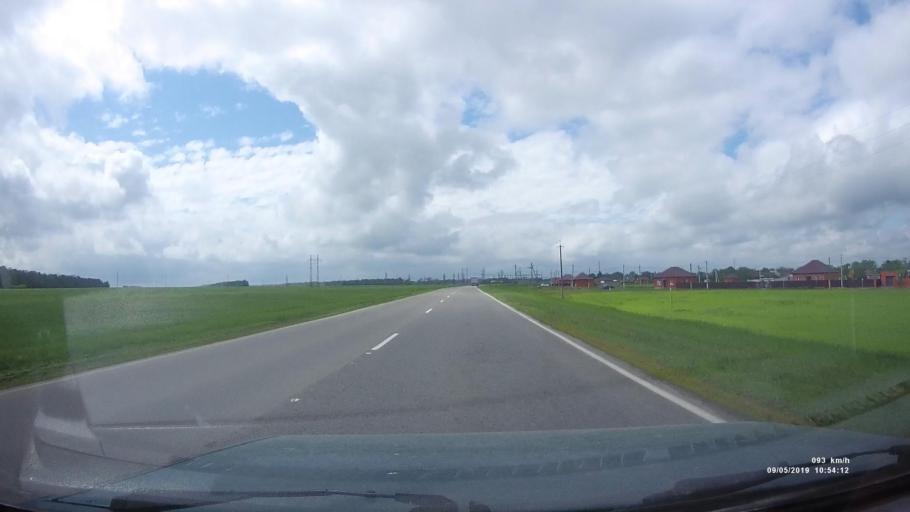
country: RU
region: Rostov
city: Peshkovo
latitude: 46.8801
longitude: 39.3333
